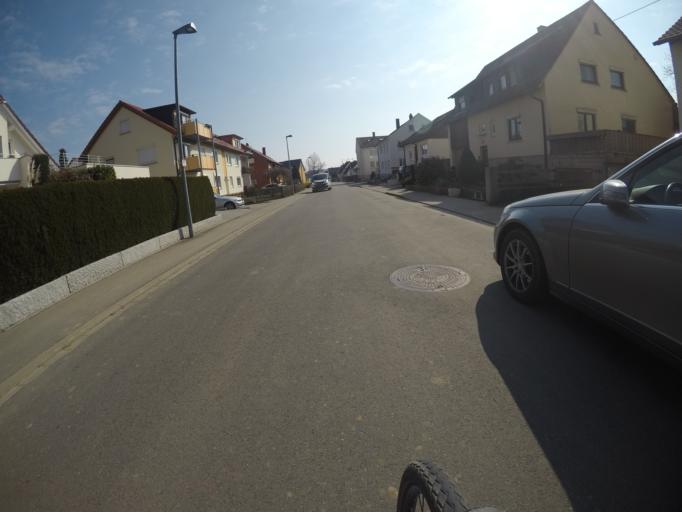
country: DE
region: Baden-Wuerttemberg
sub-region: Regierungsbezirk Stuttgart
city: Wolfschlugen
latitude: 48.6497
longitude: 9.2858
